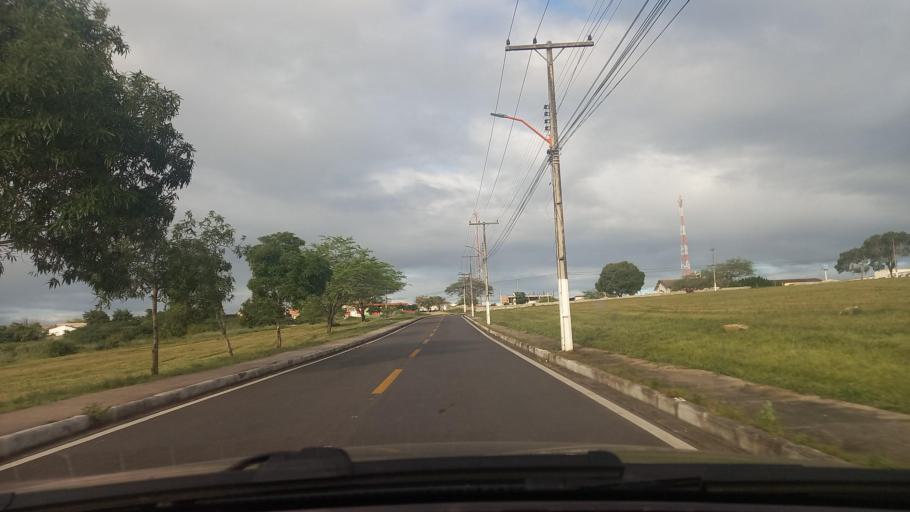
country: BR
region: Sergipe
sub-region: Caninde De Sao Francisco
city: Caninde de Sao Francisco
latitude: -9.6076
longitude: -37.7648
